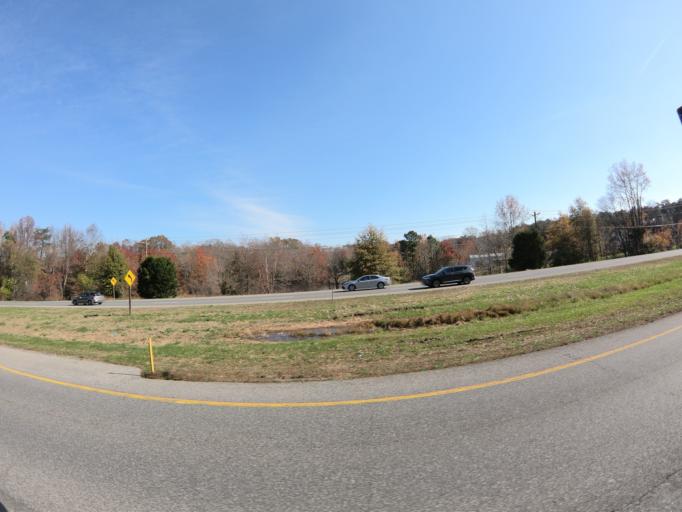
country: US
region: Maryland
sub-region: Charles County
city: Hughesville
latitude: 38.5137
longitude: -76.7749
